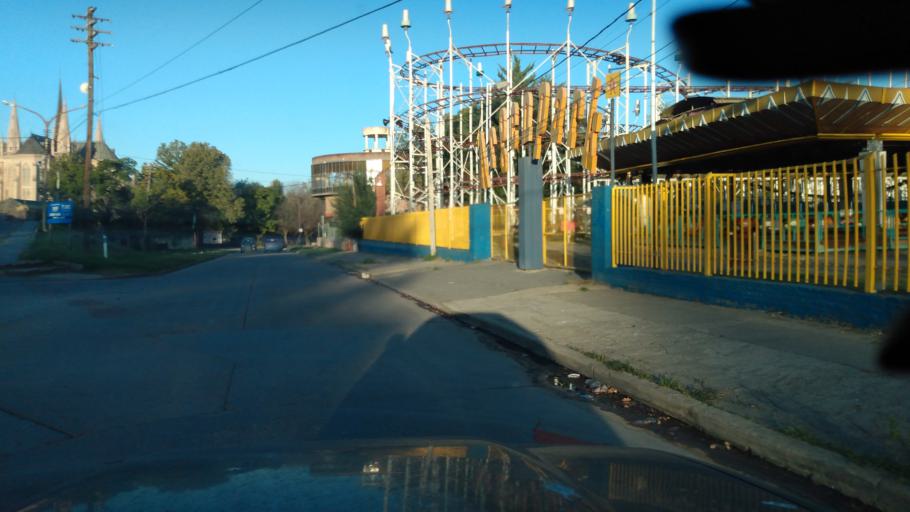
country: AR
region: Buenos Aires
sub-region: Partido de Lujan
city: Lujan
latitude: -34.5646
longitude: -59.1254
